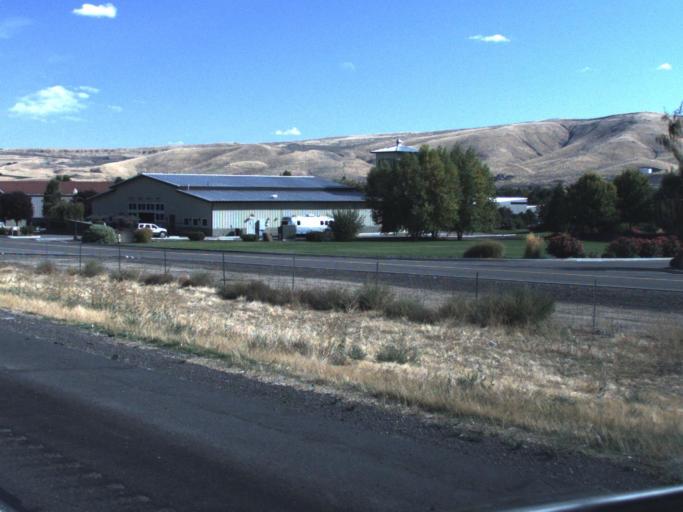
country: US
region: Washington
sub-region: Benton County
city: Prosser
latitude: 46.2212
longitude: -119.7781
